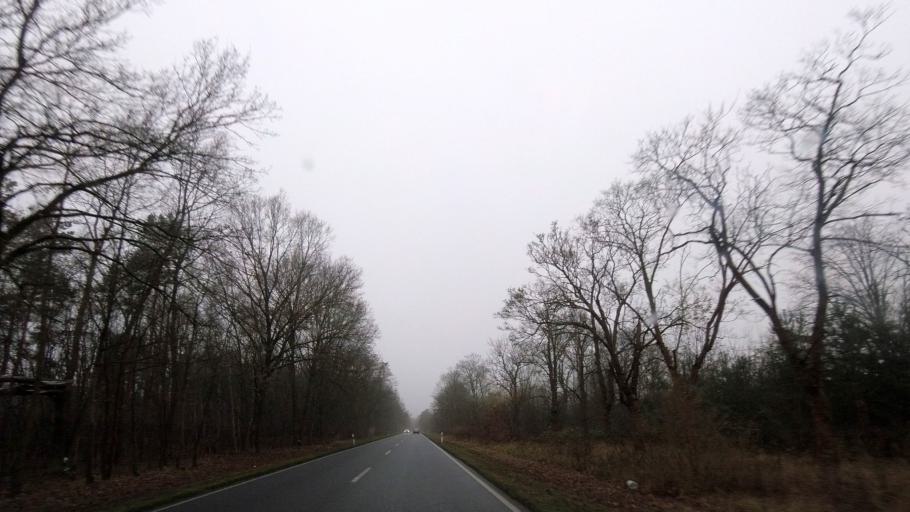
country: DE
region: Brandenburg
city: Niedergorsdorf
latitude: 52.0216
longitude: 12.9839
